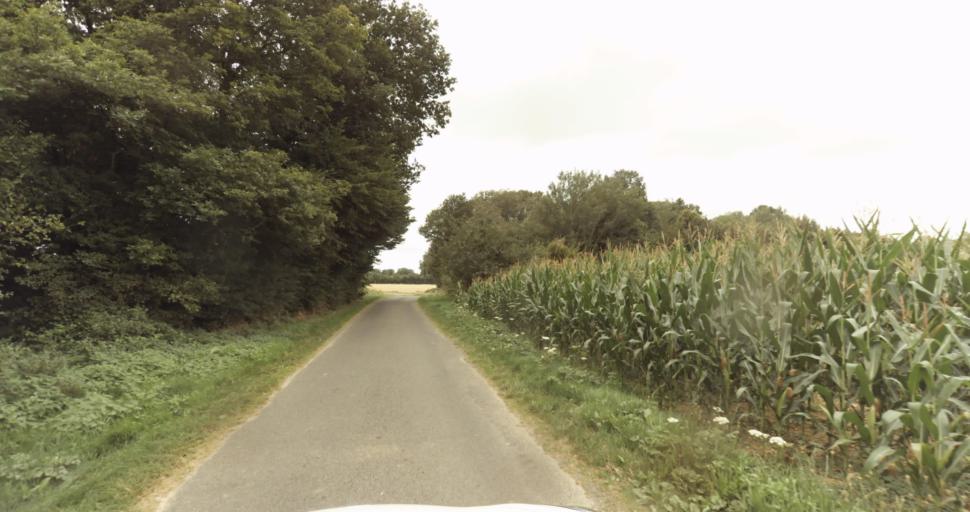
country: FR
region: Haute-Normandie
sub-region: Departement de l'Eure
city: Saint-Germain-sur-Avre
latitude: 48.8439
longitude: 1.2480
